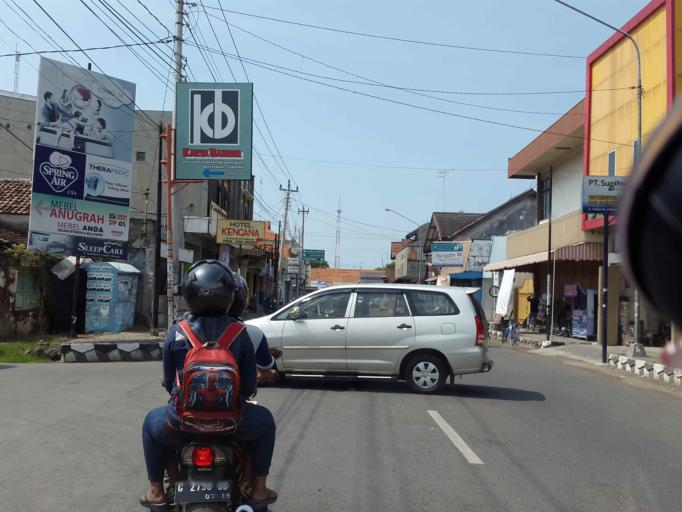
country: ID
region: Central Java
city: Pemalang
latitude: -6.8915
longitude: 109.3885
